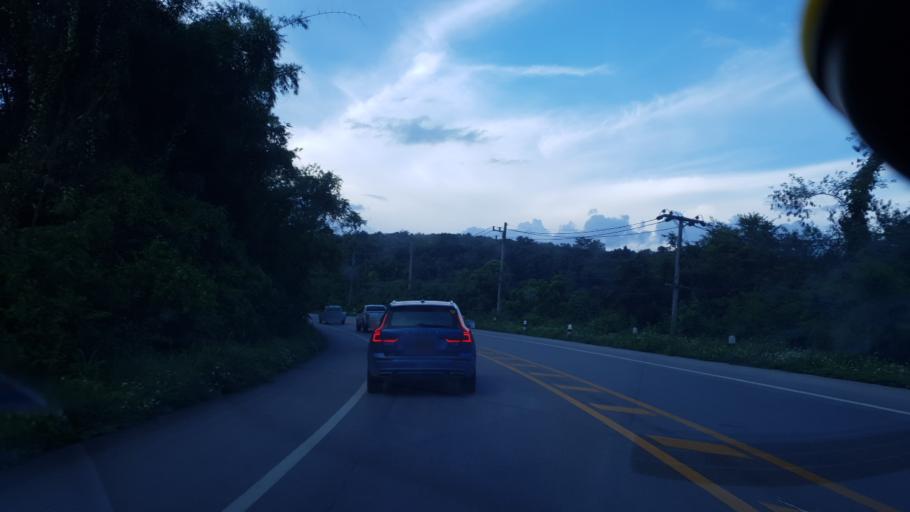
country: TH
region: Chiang Rai
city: Mae Suai
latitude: 19.6902
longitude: 99.5718
